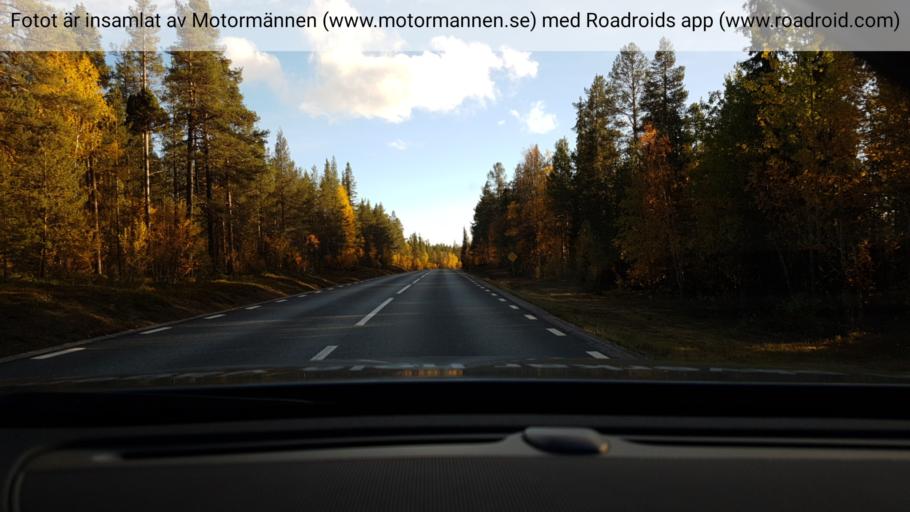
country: SE
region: Norrbotten
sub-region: Jokkmokks Kommun
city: Jokkmokk
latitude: 66.9163
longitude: 19.8323
